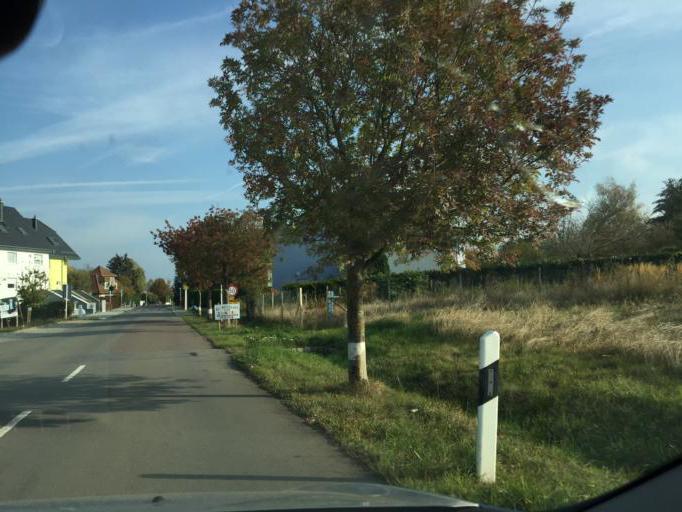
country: LU
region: Luxembourg
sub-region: Canton de Luxembourg
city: Contern
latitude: 49.5782
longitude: 6.2225
